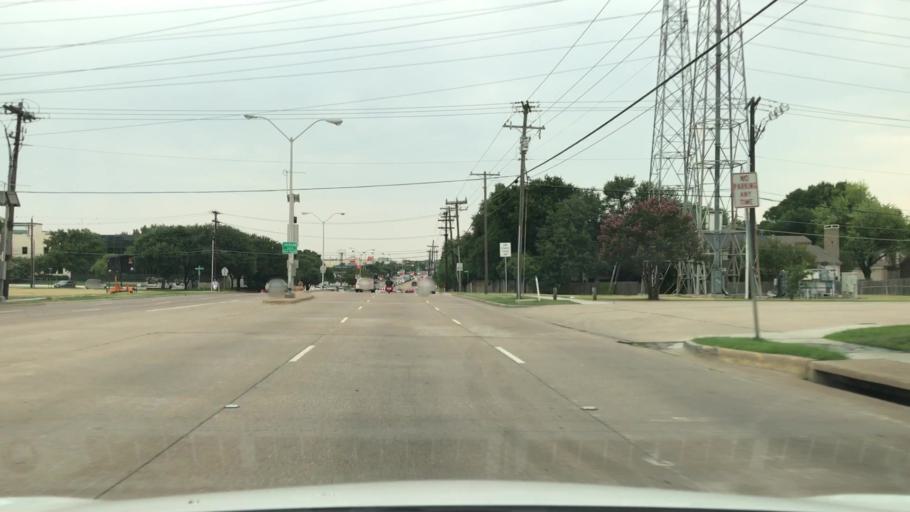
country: US
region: Texas
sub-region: Dallas County
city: Carrollton
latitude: 32.9781
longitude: -96.8902
